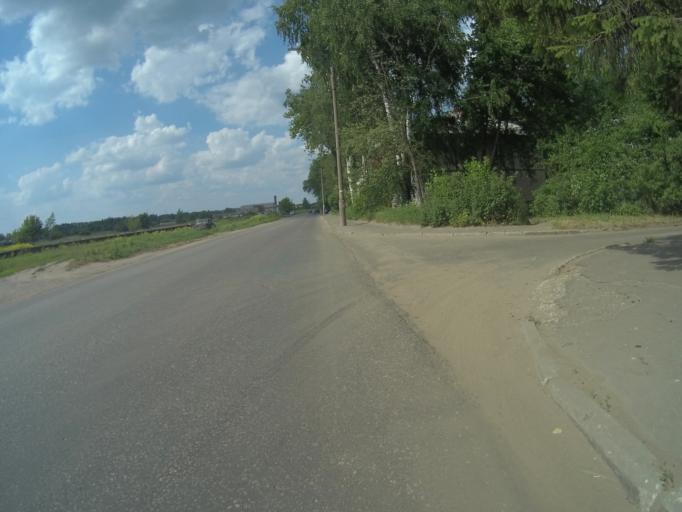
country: RU
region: Vladimir
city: Suzdal'
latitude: 56.4392
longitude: 40.4547
